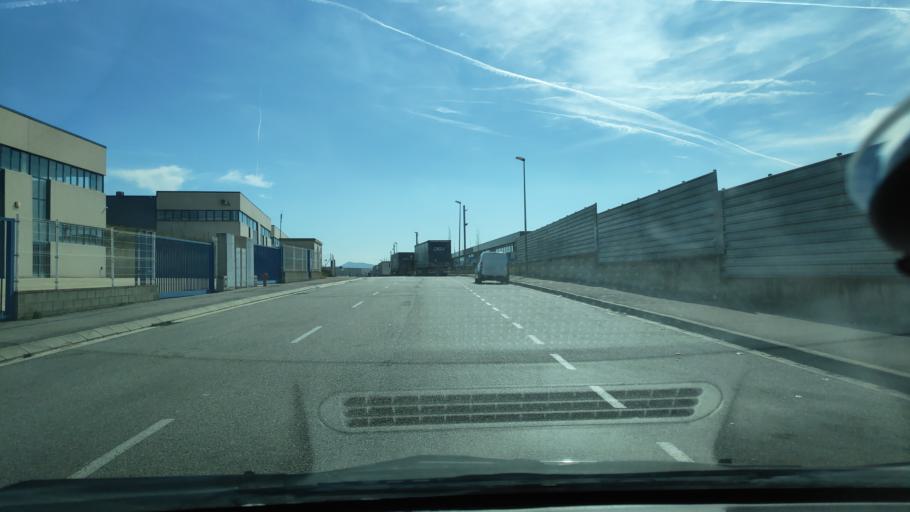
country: ES
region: Catalonia
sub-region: Provincia de Barcelona
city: Rubi
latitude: 41.5117
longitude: 2.0381
